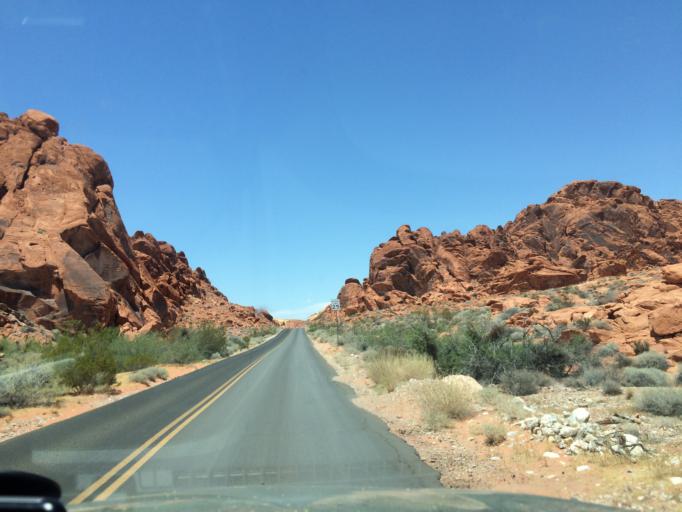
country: US
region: Nevada
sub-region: Clark County
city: Moapa Valley
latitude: 36.4419
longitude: -114.5166
